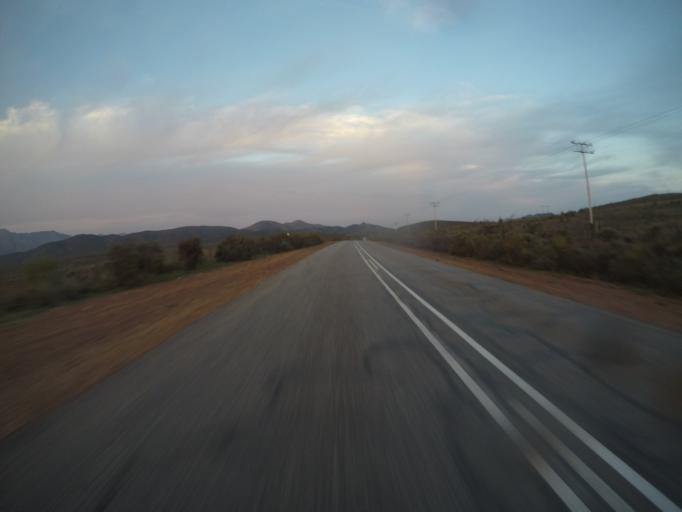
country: ZA
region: Western Cape
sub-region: Eden District Municipality
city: Plettenberg Bay
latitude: -33.7428
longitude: 23.4615
